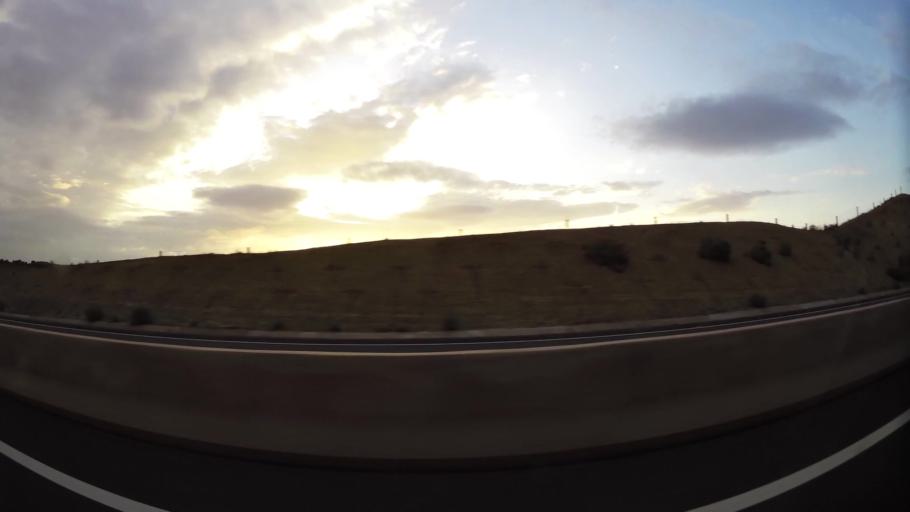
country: MA
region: Oriental
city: Taourirt
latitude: 34.4955
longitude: -2.9680
